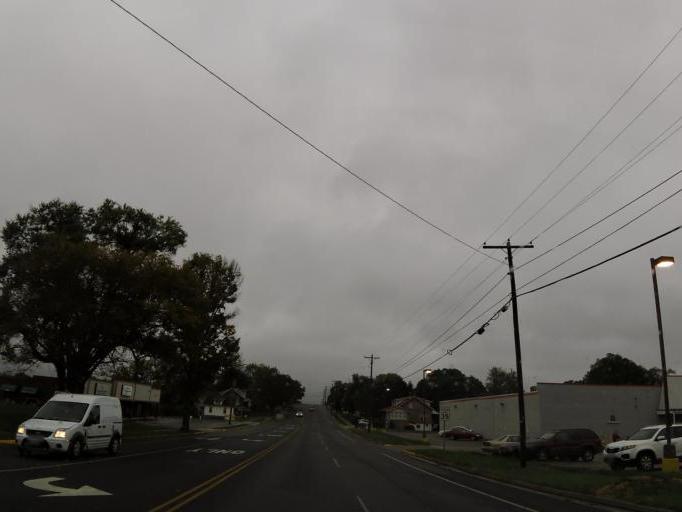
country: US
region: Virginia
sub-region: Wythe County
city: Wytheville
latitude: 36.9455
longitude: -81.0892
